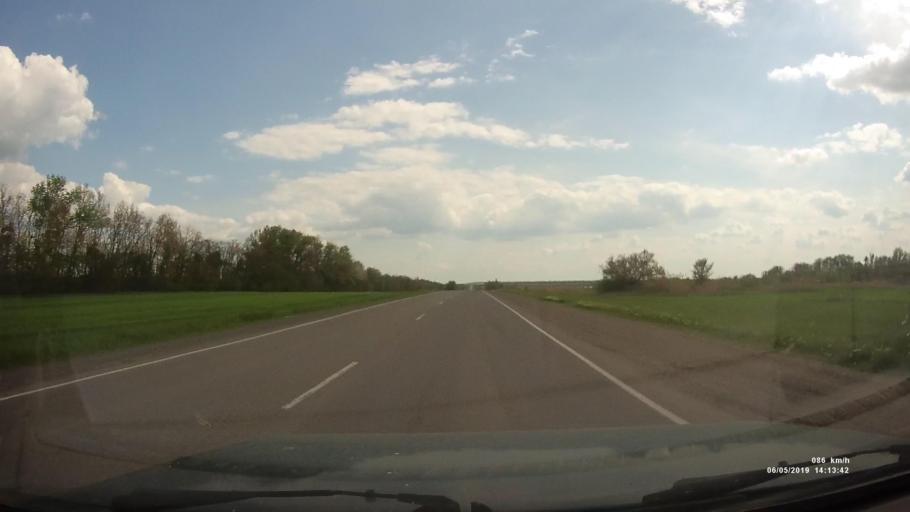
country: RU
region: Rostov
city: Kamenolomni
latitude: 47.6577
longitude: 40.2938
